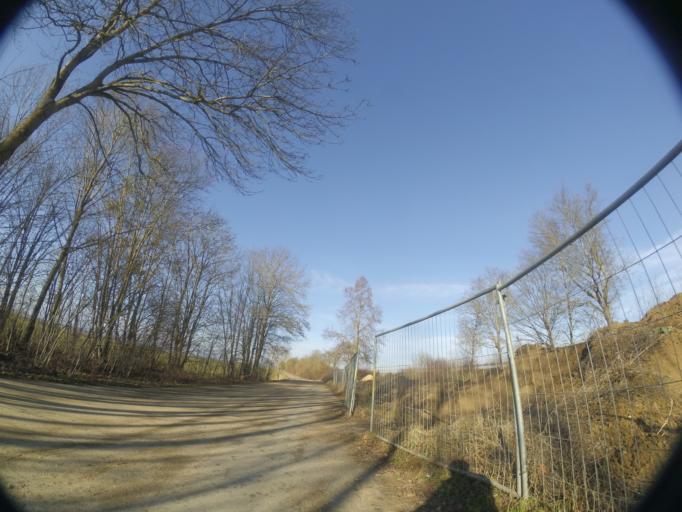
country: DE
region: Baden-Wuerttemberg
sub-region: Tuebingen Region
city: Dornstadt
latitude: 48.4747
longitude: 9.9391
